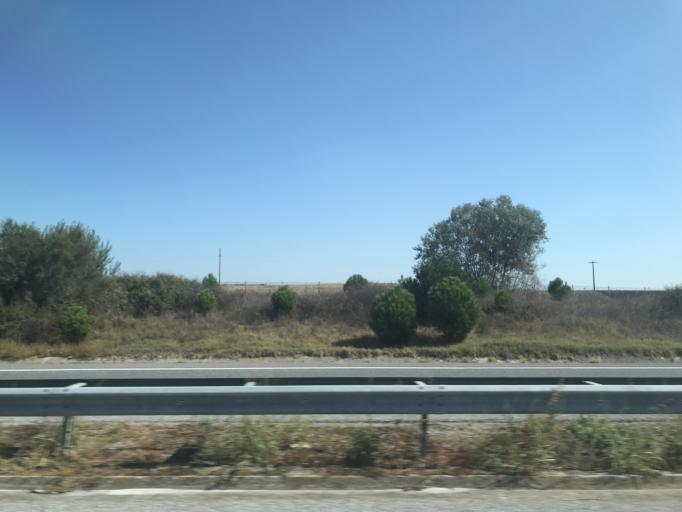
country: TR
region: Kirklareli
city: Luleburgaz
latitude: 41.4294
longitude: 27.3845
